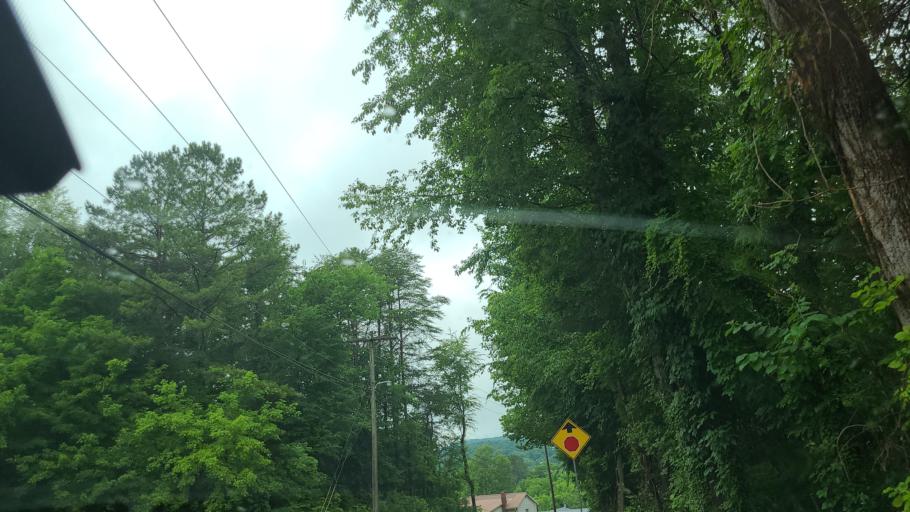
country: US
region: Tennessee
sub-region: Rhea County
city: Dayton
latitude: 35.5052
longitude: -84.9993
